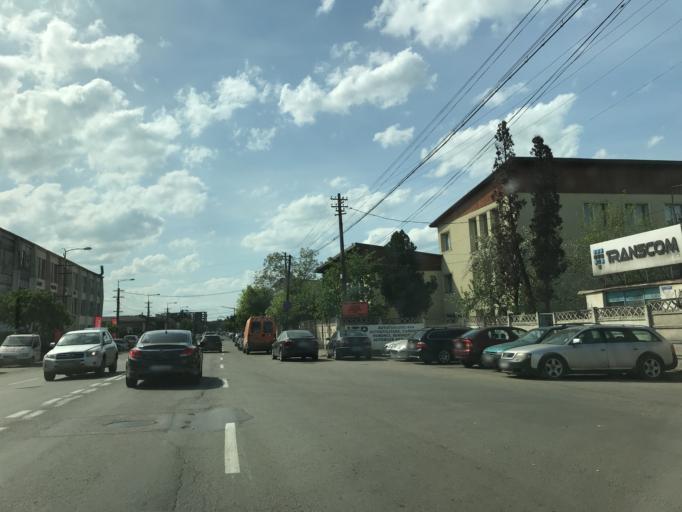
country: RO
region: Cluj
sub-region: Municipiul Cluj-Napoca
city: Cluj-Napoca
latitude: 46.7879
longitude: 23.6253
